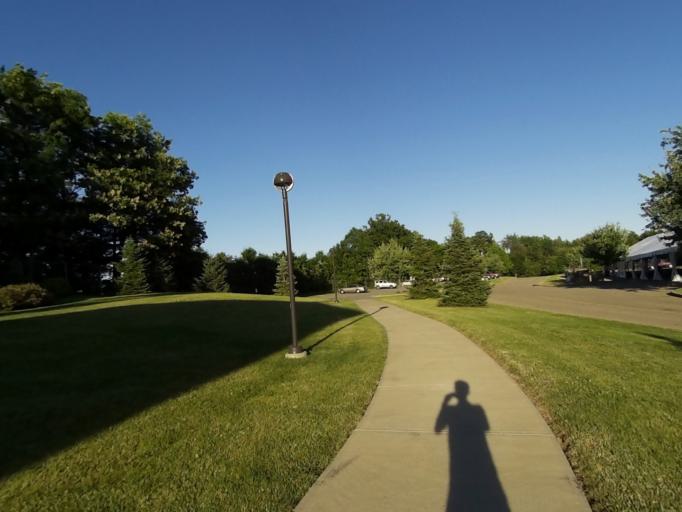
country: US
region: Ohio
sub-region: Jefferson County
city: Steubenville
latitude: 40.3794
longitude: -80.6204
